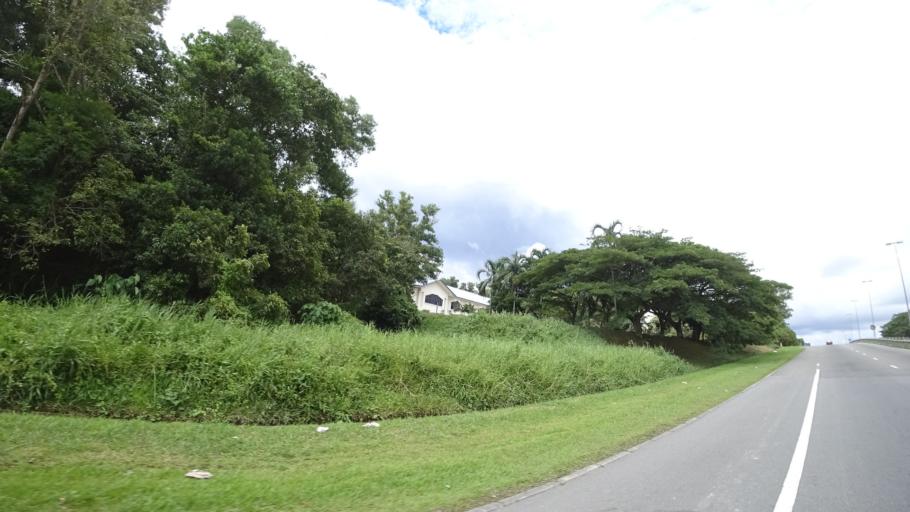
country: BN
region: Brunei and Muara
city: Bandar Seri Begawan
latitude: 4.8793
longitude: 114.8792
